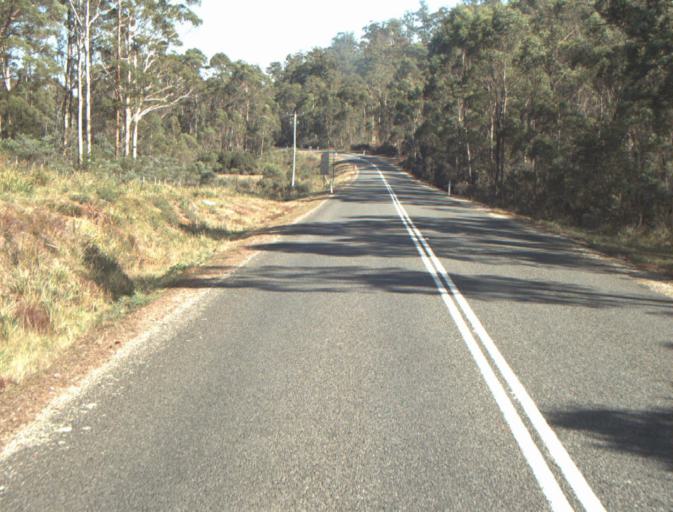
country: AU
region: Tasmania
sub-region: Launceston
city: Mayfield
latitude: -41.3289
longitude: 147.1812
